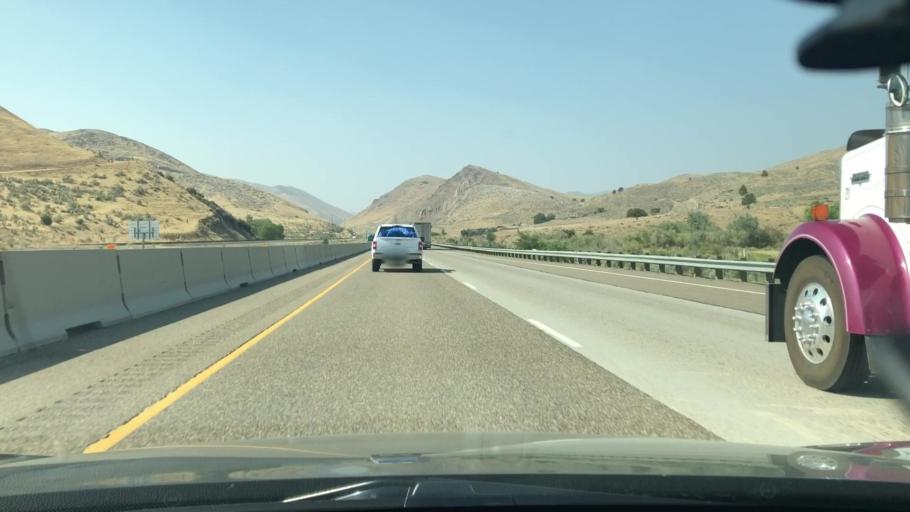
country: US
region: Idaho
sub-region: Washington County
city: Weiser
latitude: 44.4172
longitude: -117.3088
